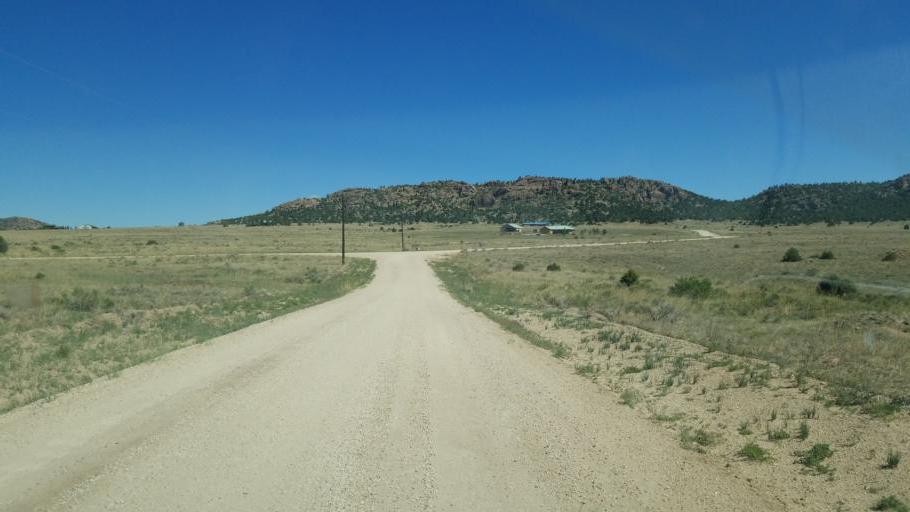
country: US
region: Colorado
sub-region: Custer County
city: Westcliffe
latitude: 38.2250
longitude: -105.4582
